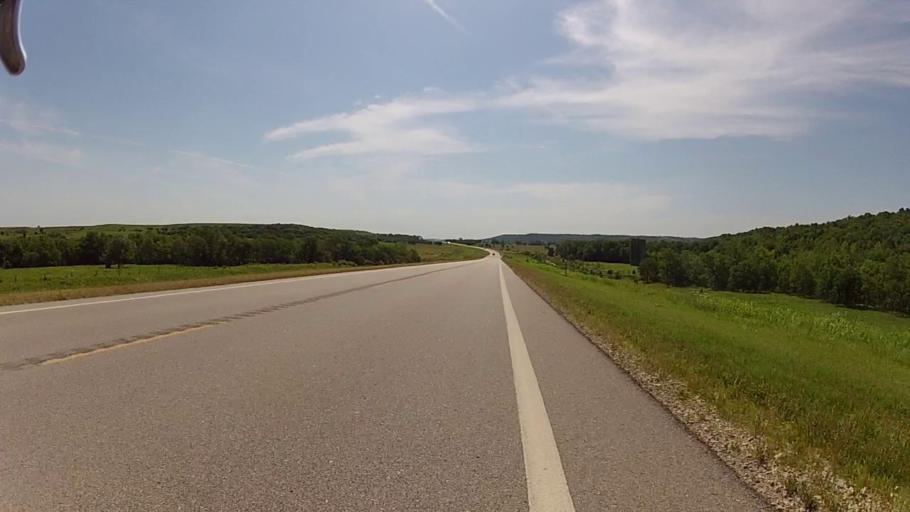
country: US
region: Kansas
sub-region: Chautauqua County
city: Sedan
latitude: 37.1093
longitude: -96.5899
